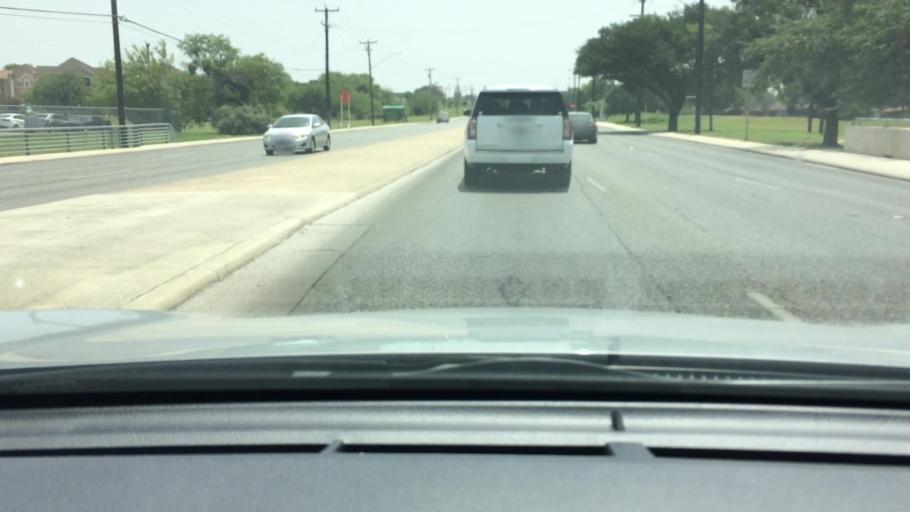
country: US
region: Texas
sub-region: Bexar County
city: San Antonio
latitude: 29.3517
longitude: -98.4474
